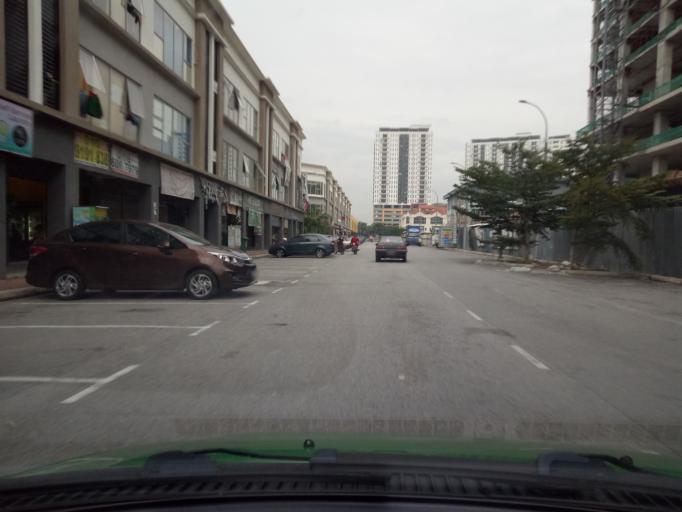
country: MY
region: Selangor
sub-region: Hulu Langat
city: Semenyih
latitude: 2.9276
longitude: 101.8590
